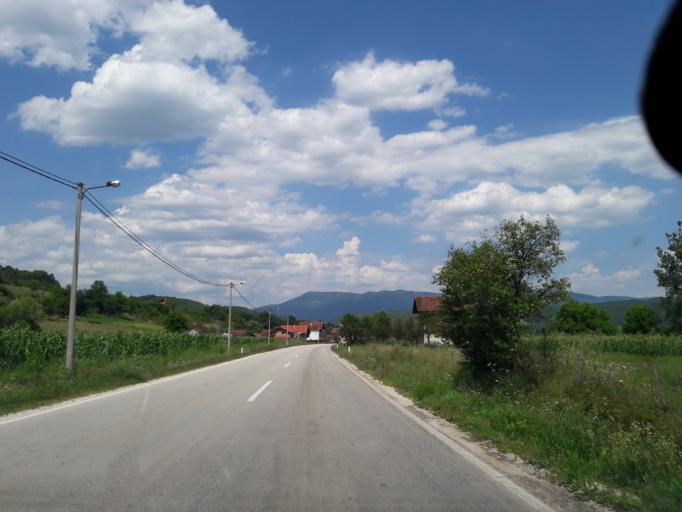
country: BA
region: Republika Srpska
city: Mrkonjic Grad
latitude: 44.4273
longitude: 17.1353
